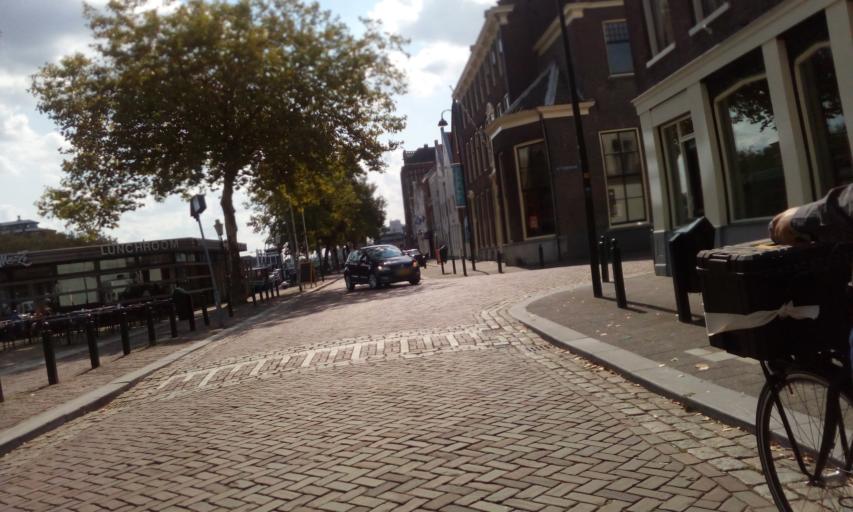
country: NL
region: South Holland
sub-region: Gemeente Vlaardingen
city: Vlaardingen
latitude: 51.9062
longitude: 4.3452
